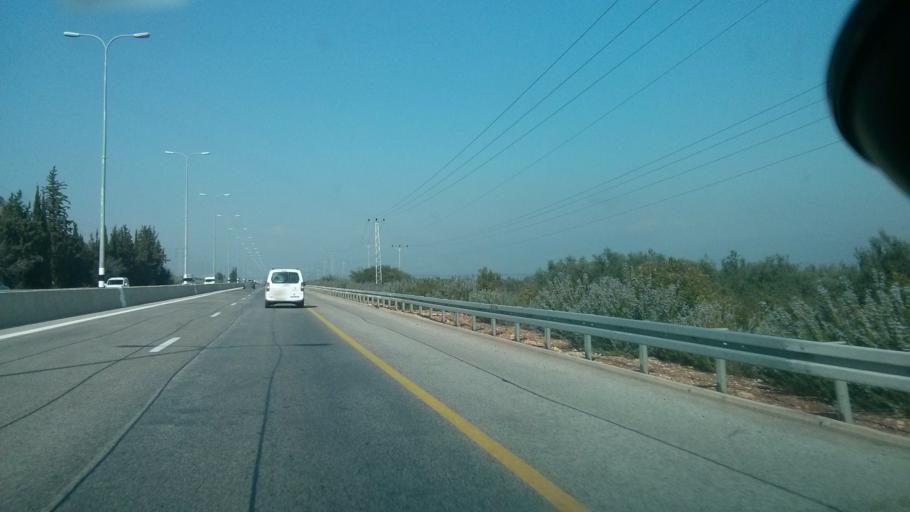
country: IL
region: Northern District
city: Rosh Pinna
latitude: 33.0637
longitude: 35.5750
